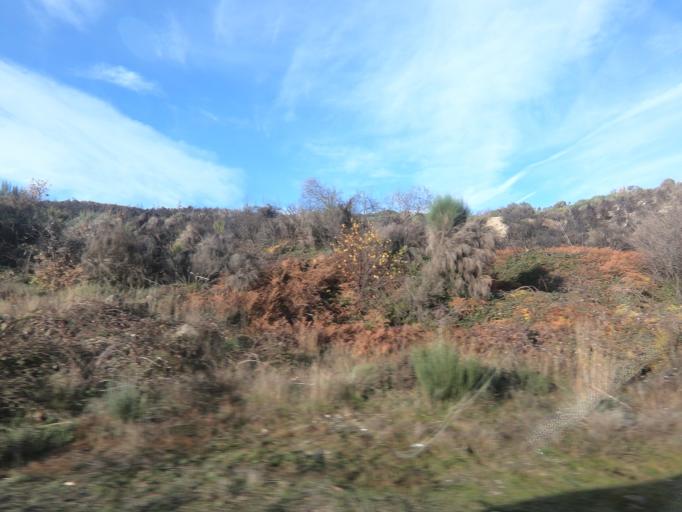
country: PT
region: Vila Real
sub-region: Sabrosa
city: Sabrosa
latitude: 41.3043
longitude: -7.6024
